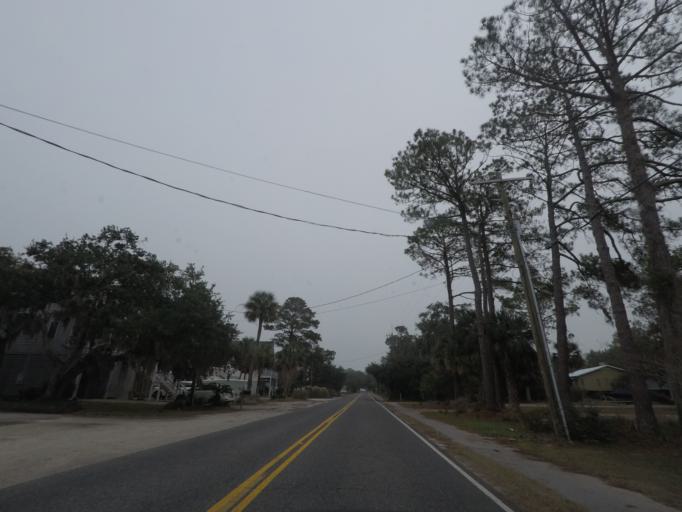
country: US
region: South Carolina
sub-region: Charleston County
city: Seabrook Island
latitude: 32.4903
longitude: -80.3263
